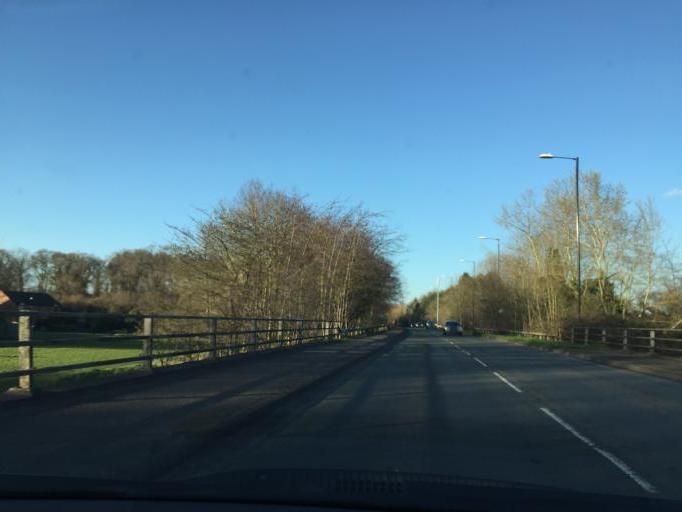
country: GB
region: England
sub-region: Warwickshire
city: Ryton on Dunsmore
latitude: 52.3978
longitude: -1.4658
